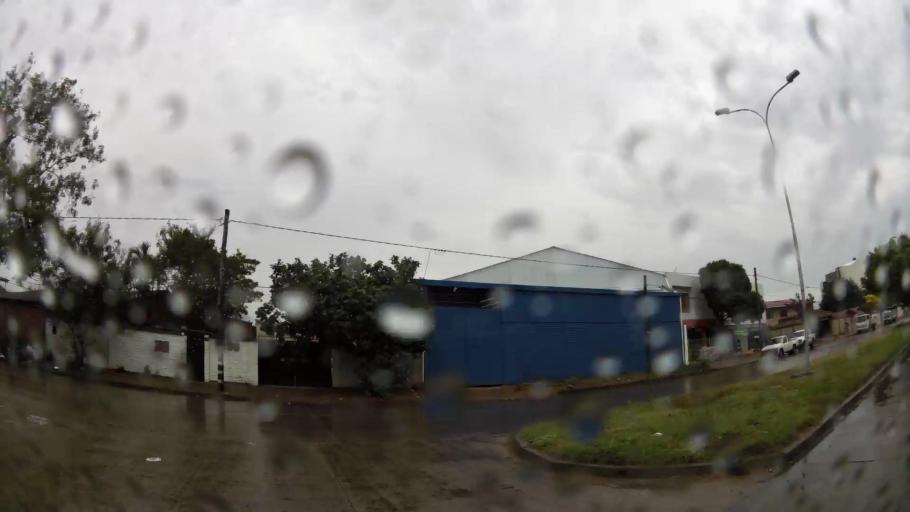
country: BO
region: Santa Cruz
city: Santa Cruz de la Sierra
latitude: -17.7832
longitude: -63.1557
